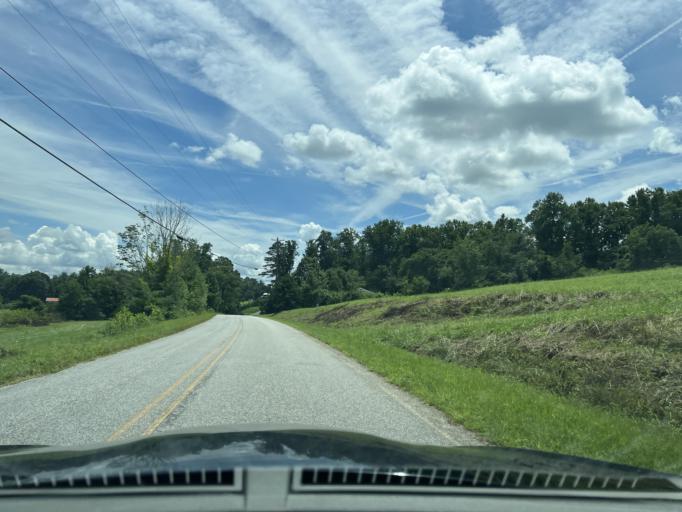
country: US
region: North Carolina
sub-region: Henderson County
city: Fruitland
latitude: 35.4032
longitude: -82.3911
